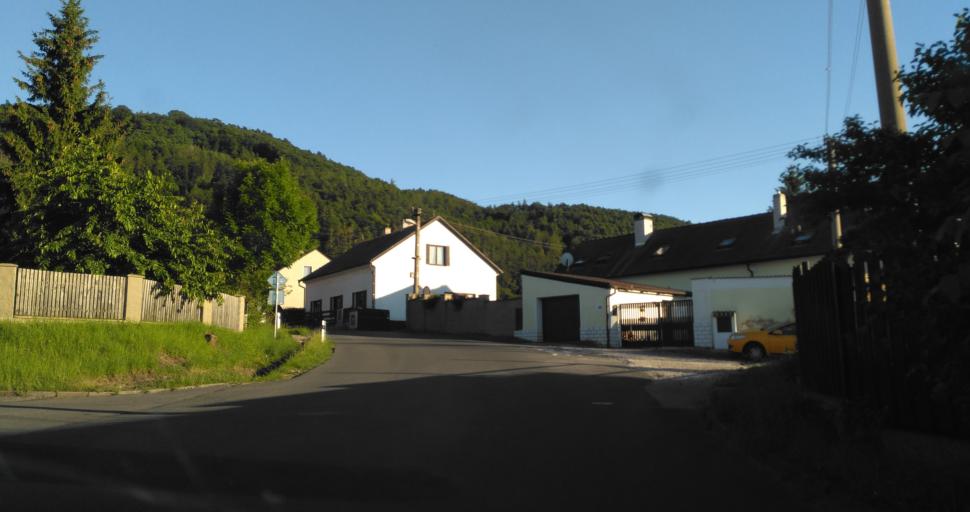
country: CZ
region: Central Bohemia
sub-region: Okres Beroun
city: Kraluv Dvur
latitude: 49.9272
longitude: 14.0208
